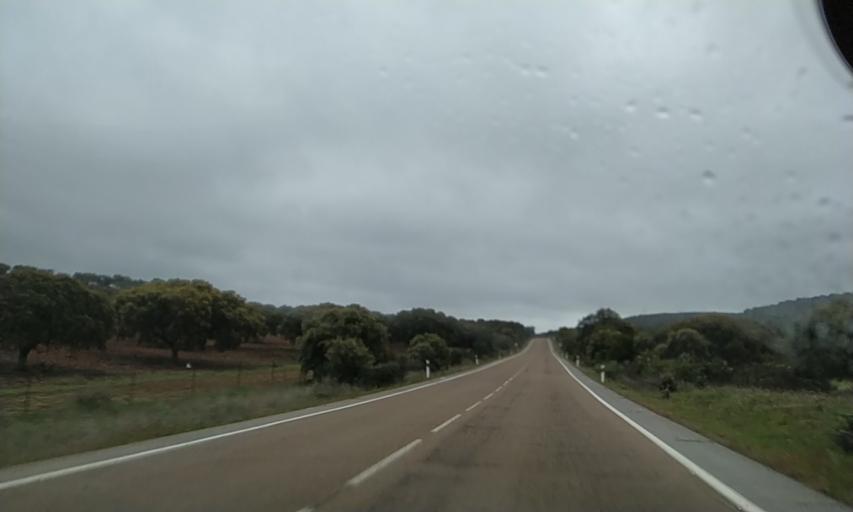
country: ES
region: Extremadura
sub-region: Provincia de Badajoz
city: Puebla de Obando
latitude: 39.2887
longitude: -6.5222
